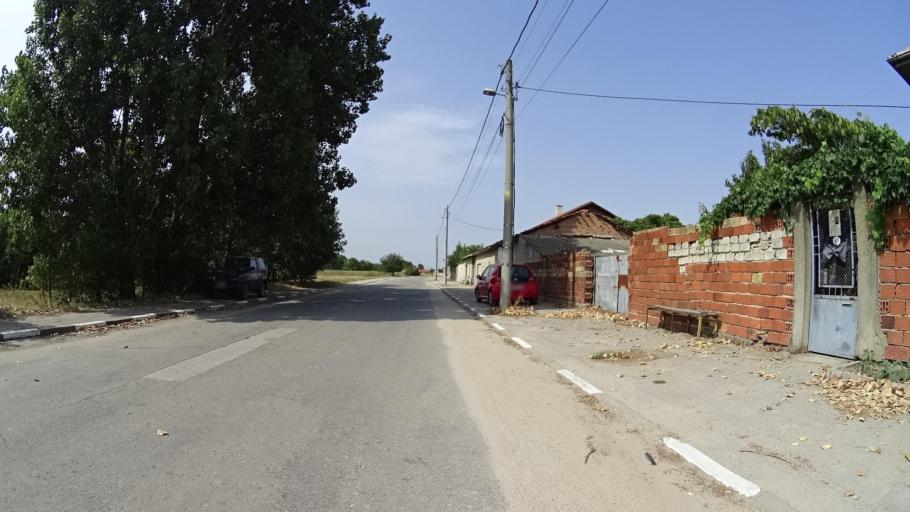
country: BG
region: Plovdiv
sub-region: Obshtina Plovdiv
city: Plovdiv
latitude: 42.2427
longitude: 24.7953
